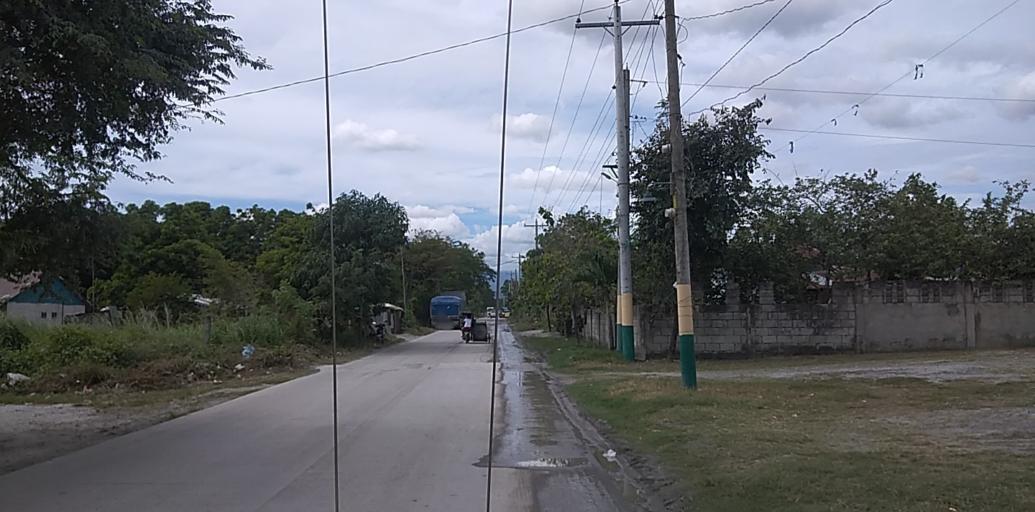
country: PH
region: Central Luzon
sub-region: Province of Pampanga
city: Balas
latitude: 15.0661
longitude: 120.5727
